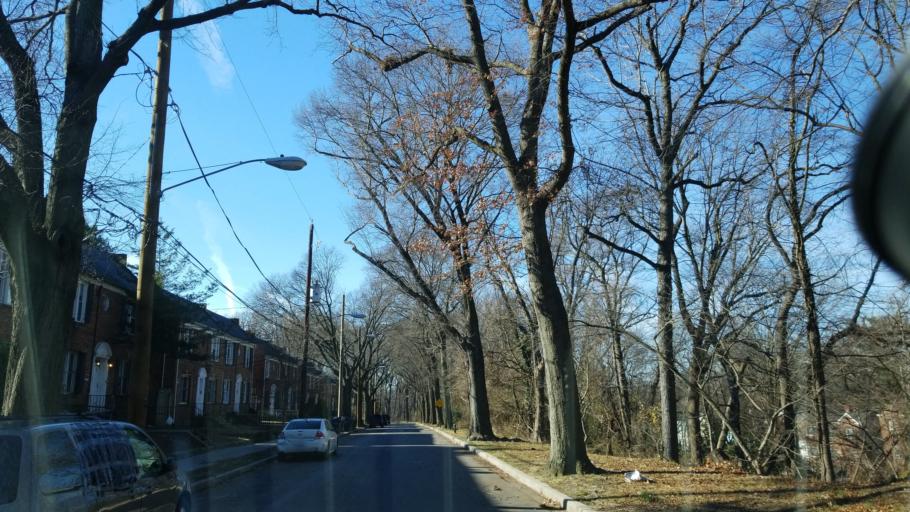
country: US
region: Maryland
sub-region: Prince George's County
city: Glassmanor
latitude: 38.8447
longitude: -77.0001
